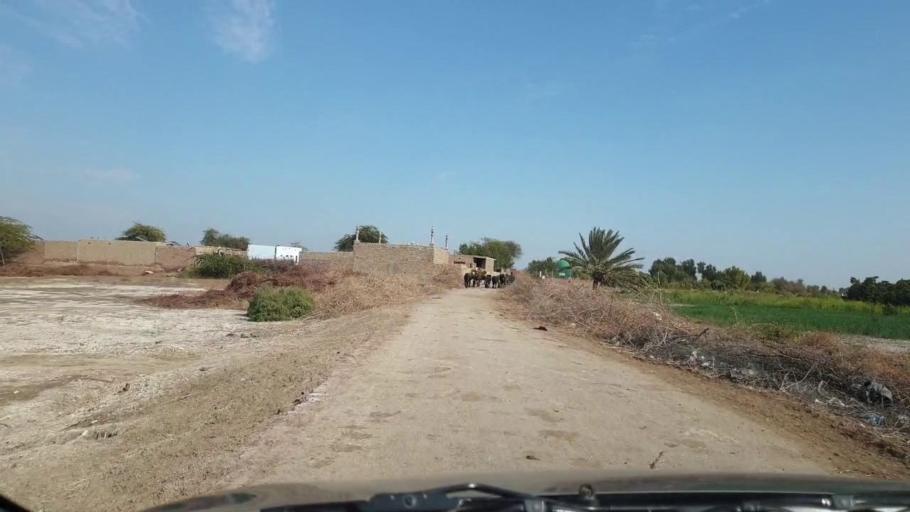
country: PK
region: Sindh
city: Sinjhoro
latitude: 26.0295
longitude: 68.8158
